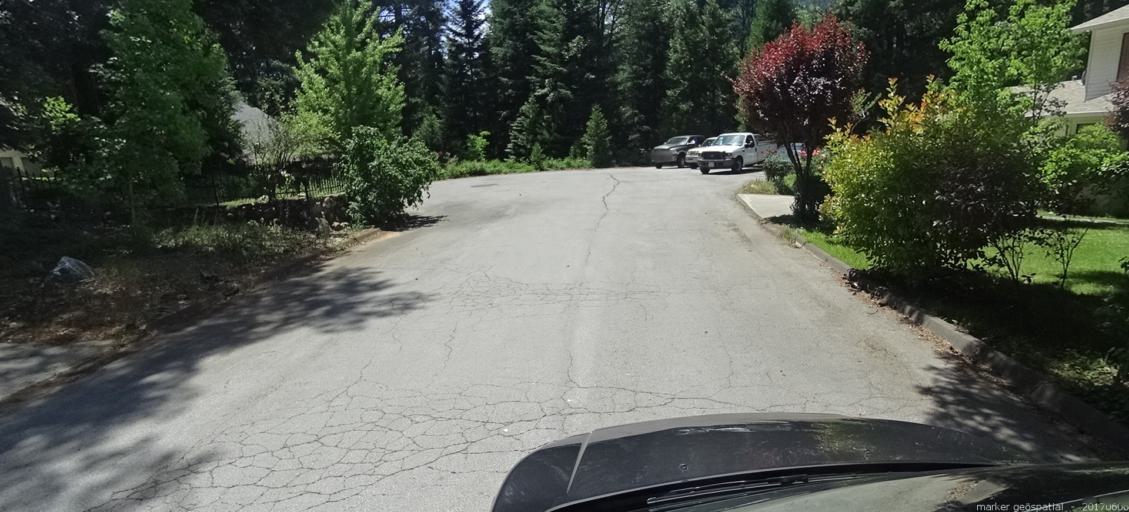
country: US
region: California
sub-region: Siskiyou County
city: Dunsmuir
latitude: 41.2300
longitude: -122.2731
